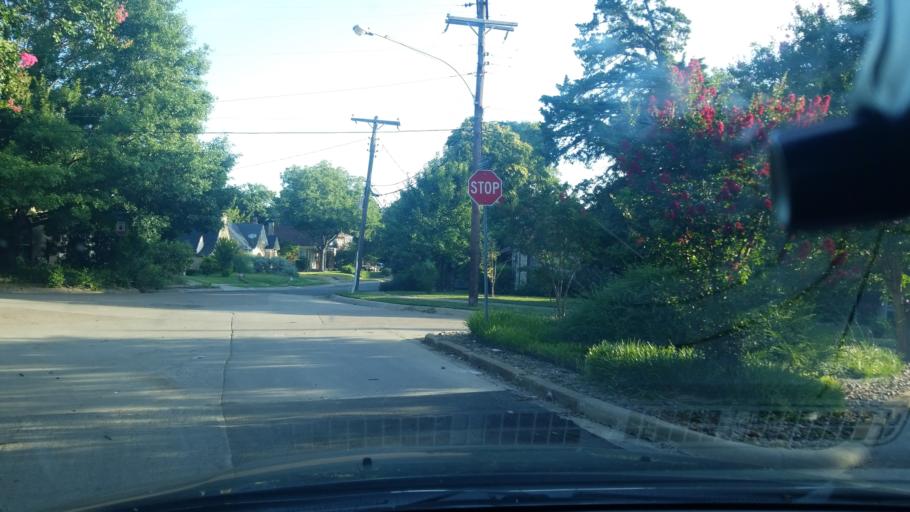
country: US
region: Texas
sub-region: Dallas County
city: Dallas
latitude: 32.7284
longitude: -96.8216
